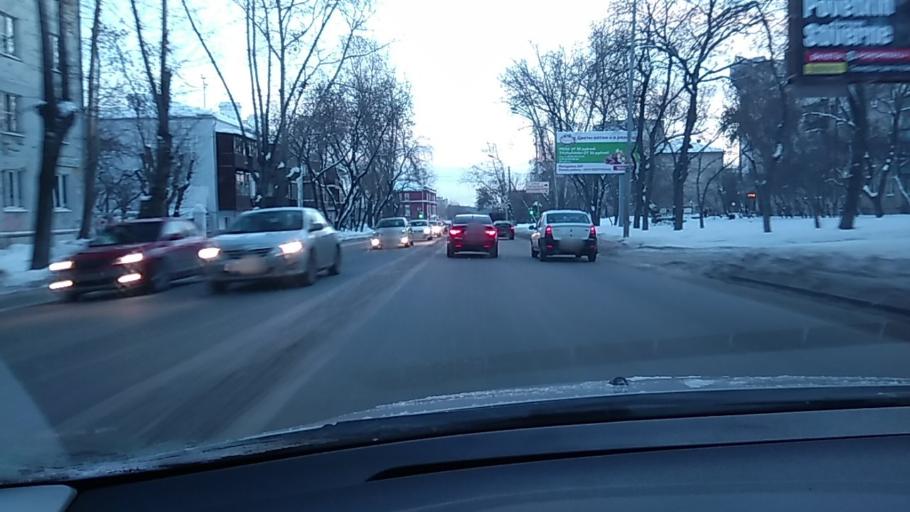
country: RU
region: Sverdlovsk
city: Yekaterinburg
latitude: 56.8247
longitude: 60.6384
